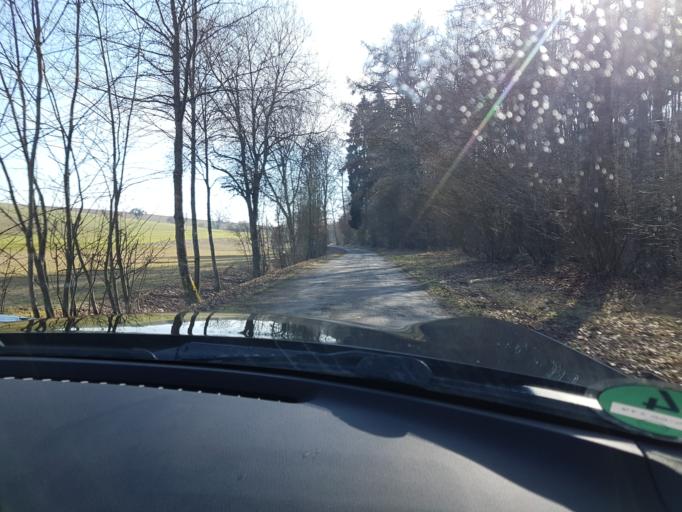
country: DE
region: Baden-Wuerttemberg
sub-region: Karlsruhe Region
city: Rosenberg
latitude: 49.4195
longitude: 9.4975
